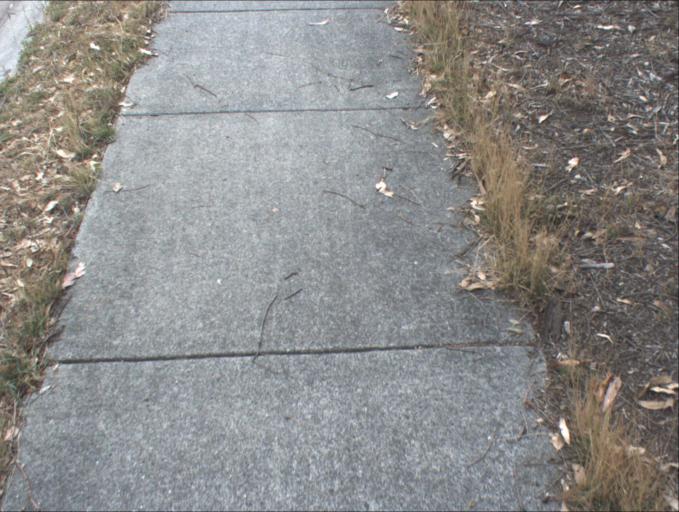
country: AU
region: Queensland
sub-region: Logan
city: Windaroo
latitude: -27.7235
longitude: 153.1873
